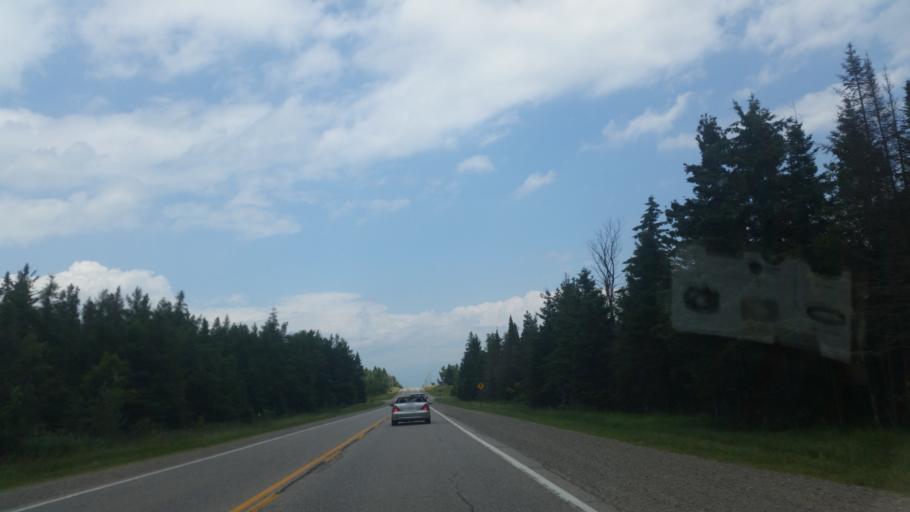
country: CA
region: Ontario
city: Orangeville
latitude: 43.7339
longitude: -80.0909
